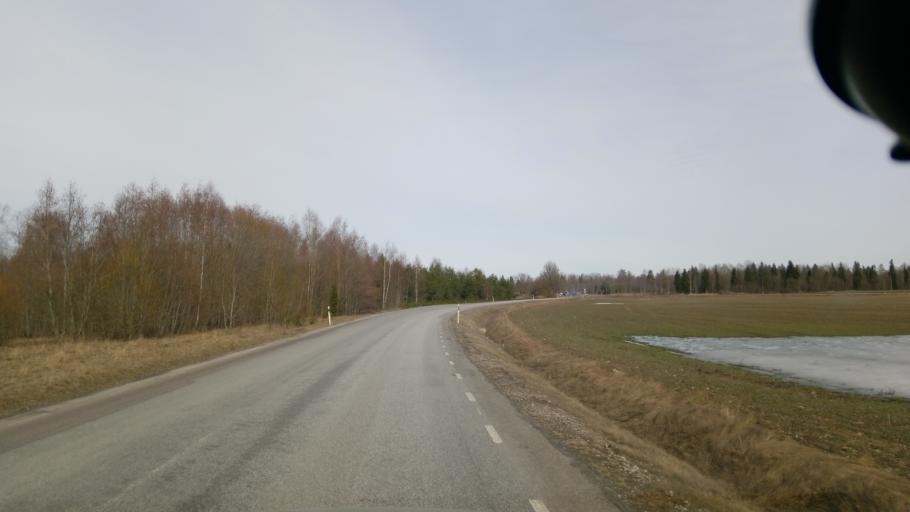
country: EE
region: Raplamaa
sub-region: Rapla vald
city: Rapla
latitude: 59.0364
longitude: 24.8357
